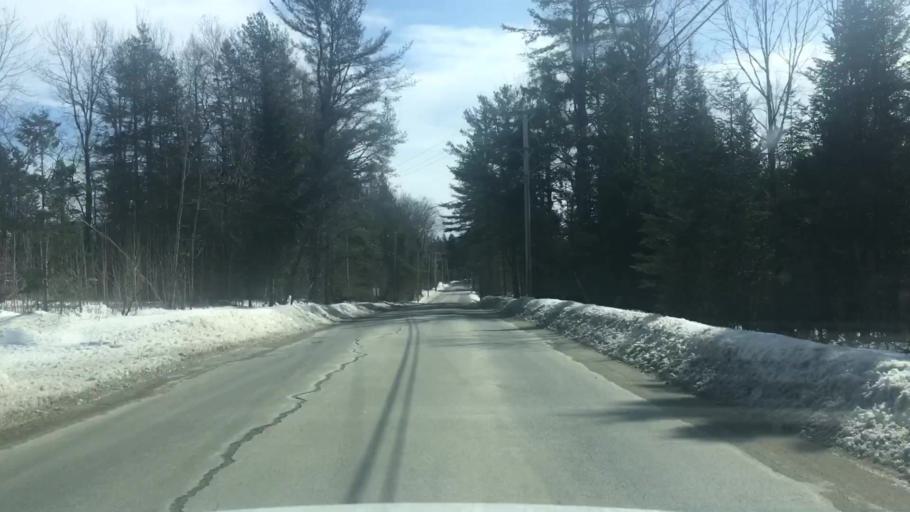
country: US
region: Maine
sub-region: Penobscot County
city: Holden
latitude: 44.7563
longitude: -68.6374
